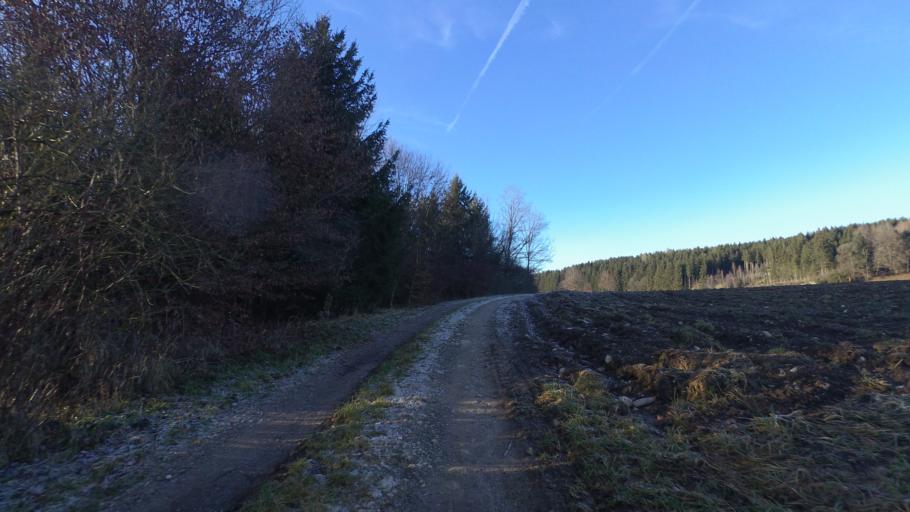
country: DE
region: Bavaria
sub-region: Upper Bavaria
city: Chieming
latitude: 47.9114
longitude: 12.5524
